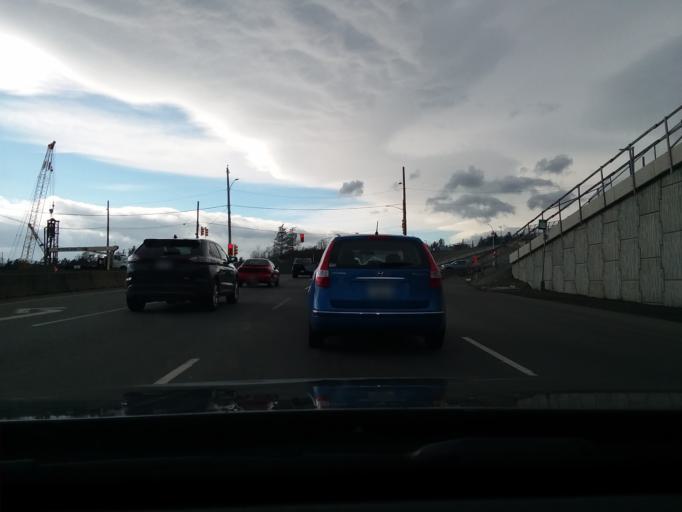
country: CA
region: British Columbia
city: Victoria
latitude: 48.4597
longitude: -123.4032
